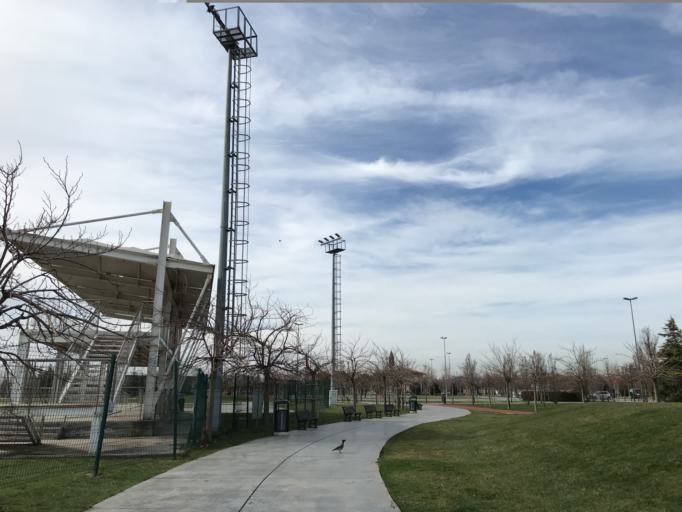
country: TR
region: Istanbul
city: Maltepe
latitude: 40.9340
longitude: 29.1143
